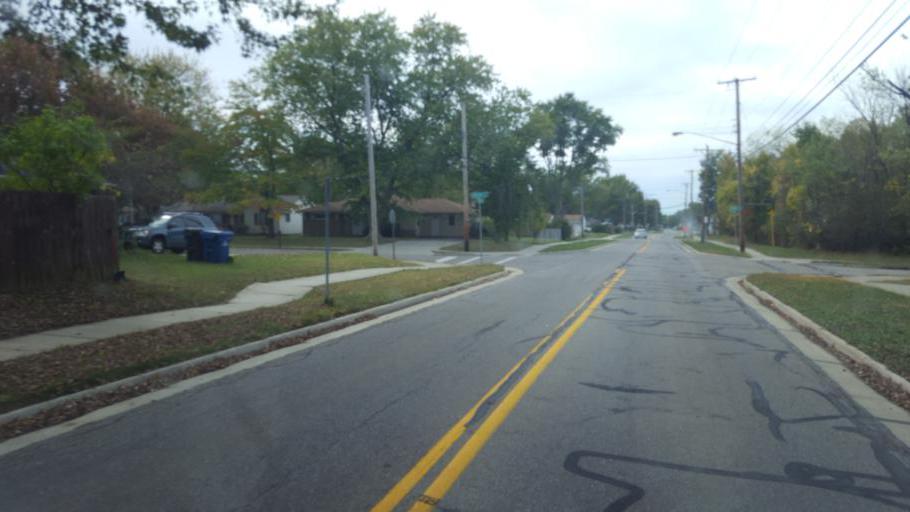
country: US
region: Ohio
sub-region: Lorain County
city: Sheffield Lake
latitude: 41.4850
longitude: -82.1108
